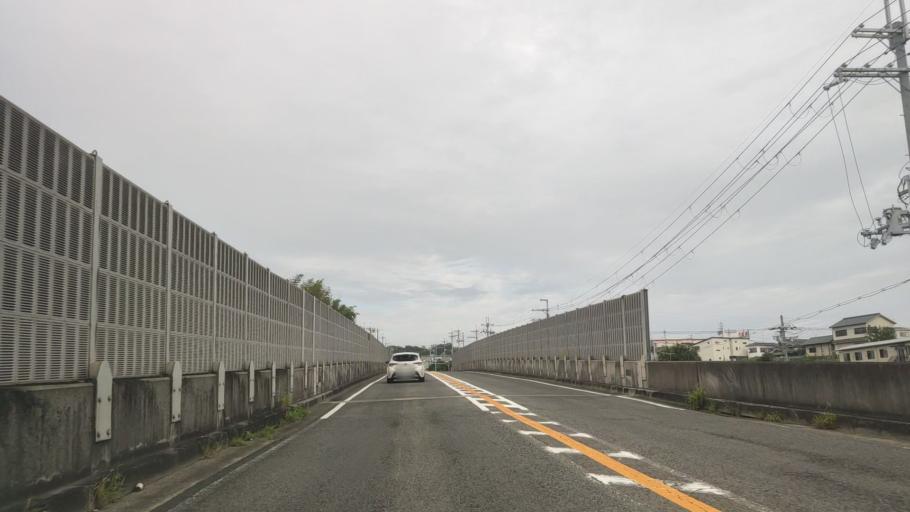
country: JP
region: Osaka
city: Tondabayashicho
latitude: 34.4432
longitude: 135.5570
